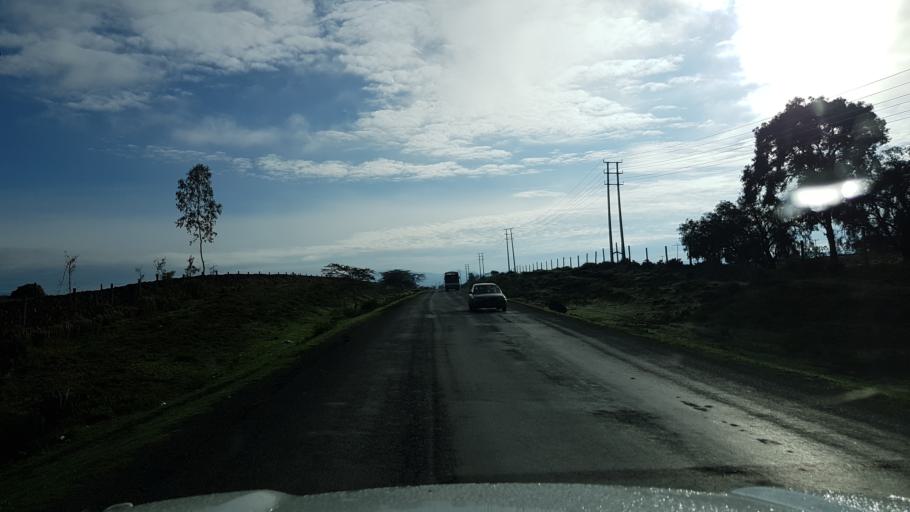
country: KE
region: Nakuru
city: Naivasha
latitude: -0.8208
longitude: 36.3864
